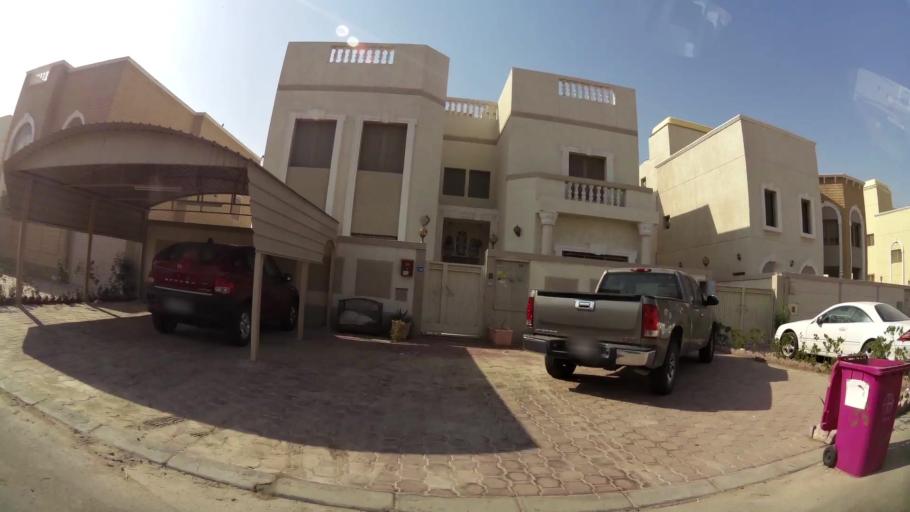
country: KW
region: Al Ahmadi
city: Al Wafrah
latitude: 28.7968
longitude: 48.0642
